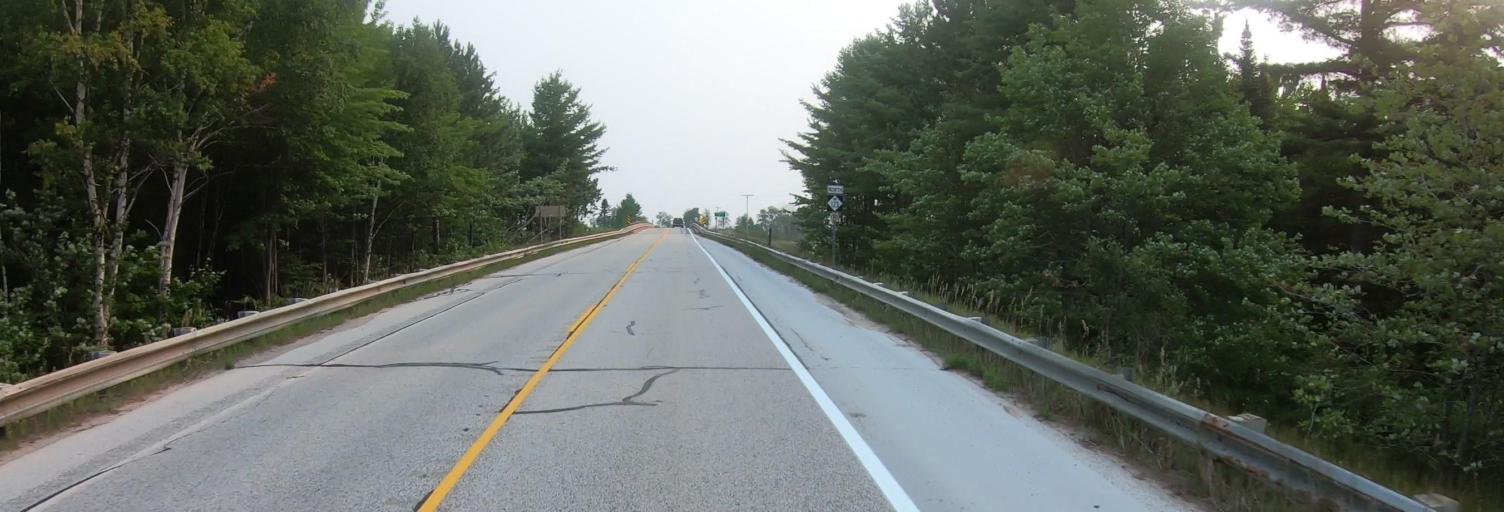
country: US
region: Michigan
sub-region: Luce County
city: Newberry
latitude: 46.5554
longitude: -85.0326
